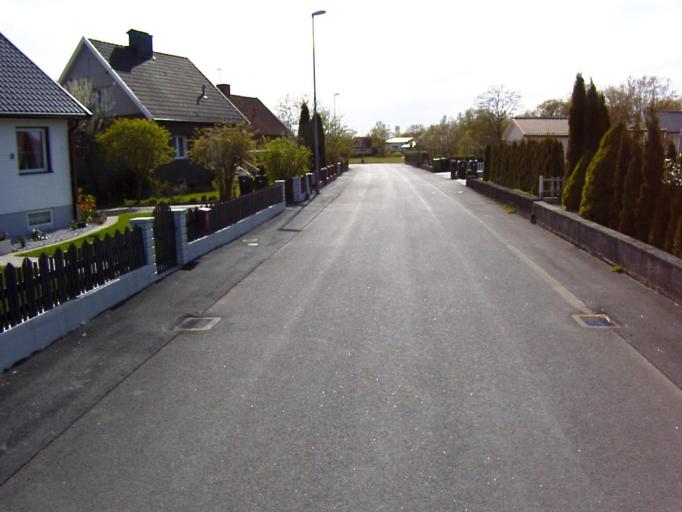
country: SE
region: Skane
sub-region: Kristianstads Kommun
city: Kristianstad
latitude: 56.0559
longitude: 14.1535
